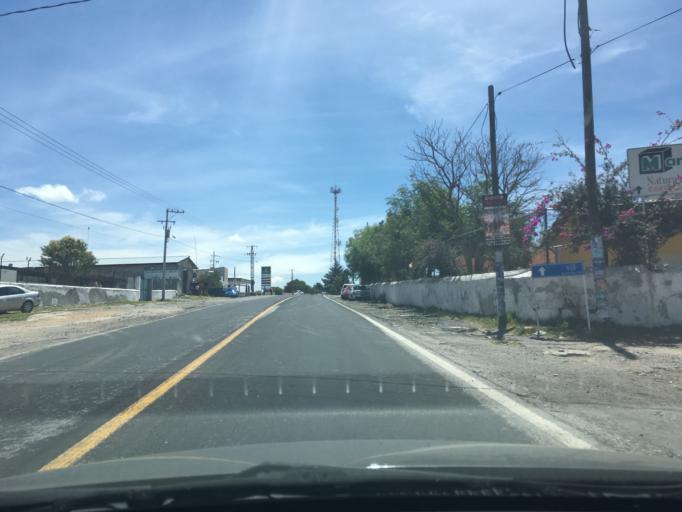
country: MX
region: Hidalgo
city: Huichapan
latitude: 20.4363
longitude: -99.5350
